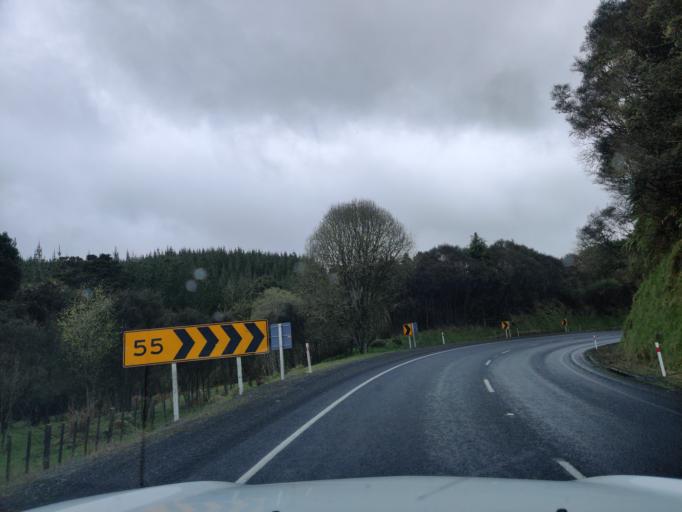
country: NZ
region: Waikato
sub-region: Otorohanga District
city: Otorohanga
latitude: -38.6576
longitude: 175.2085
